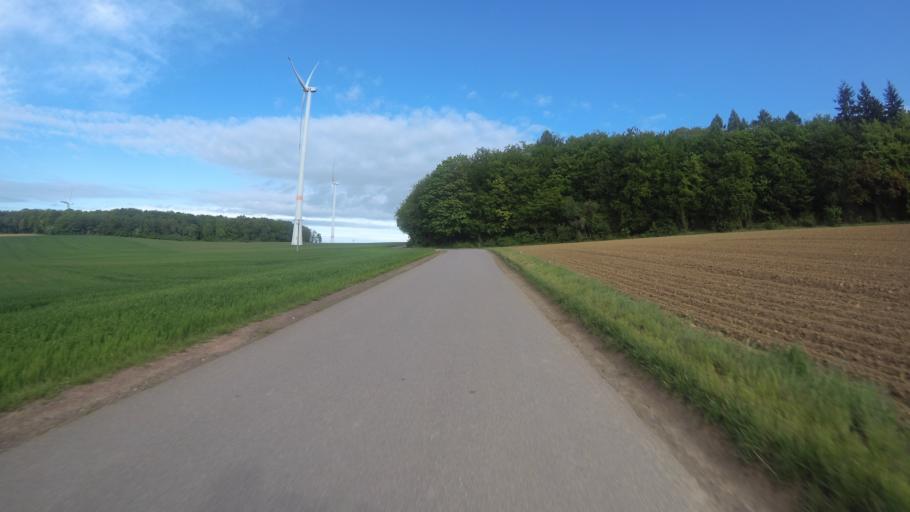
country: DE
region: Saarland
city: Orscholz
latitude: 49.4327
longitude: 6.5477
